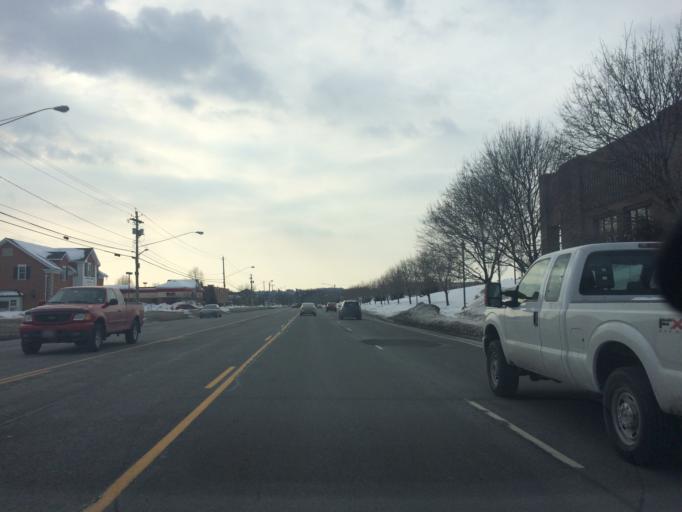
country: US
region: New York
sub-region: Monroe County
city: Pittsford
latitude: 43.1071
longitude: -77.5428
